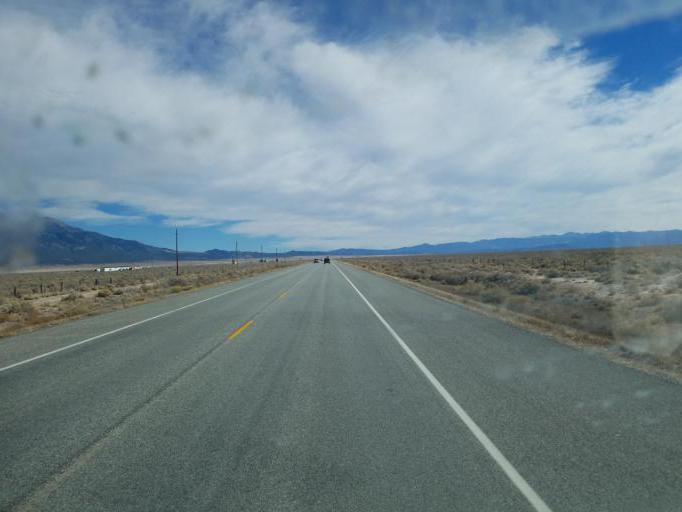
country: US
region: Colorado
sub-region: Alamosa County
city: Alamosa East
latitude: 37.4746
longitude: -105.6752
